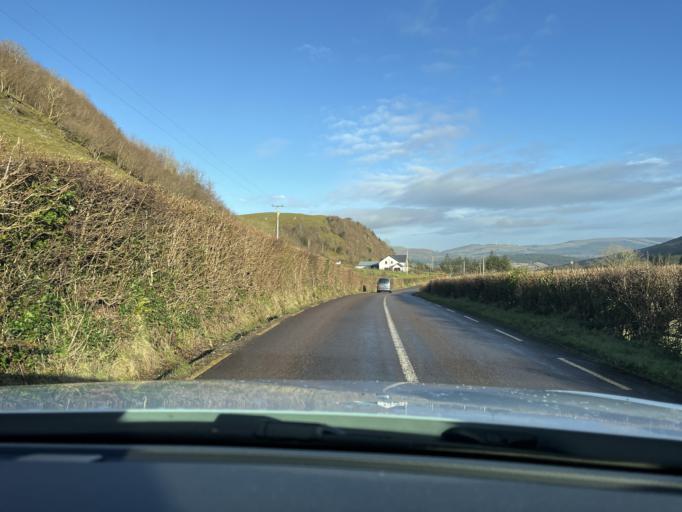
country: IE
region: Connaught
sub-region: County Leitrim
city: Manorhamilton
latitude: 54.2904
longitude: -8.2590
